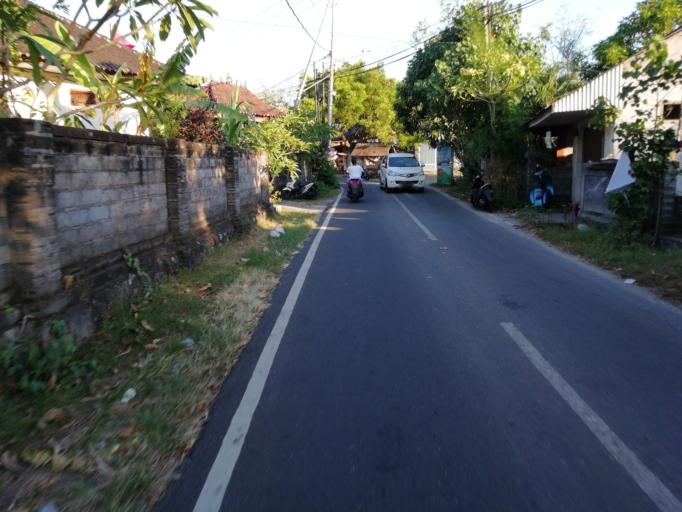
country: ID
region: Bali
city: Bualu
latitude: -8.7964
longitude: 115.1932
